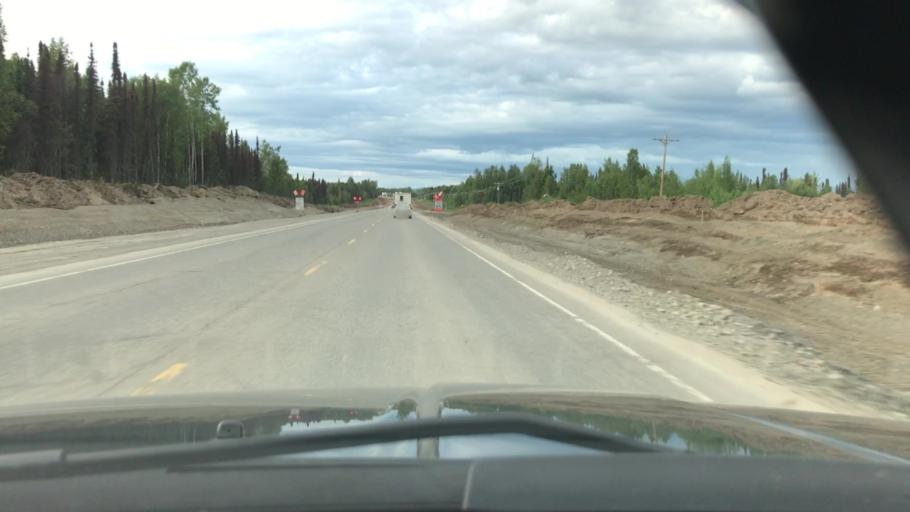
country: US
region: Alaska
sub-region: Matanuska-Susitna Borough
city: Y
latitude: 62.1193
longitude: -150.0477
